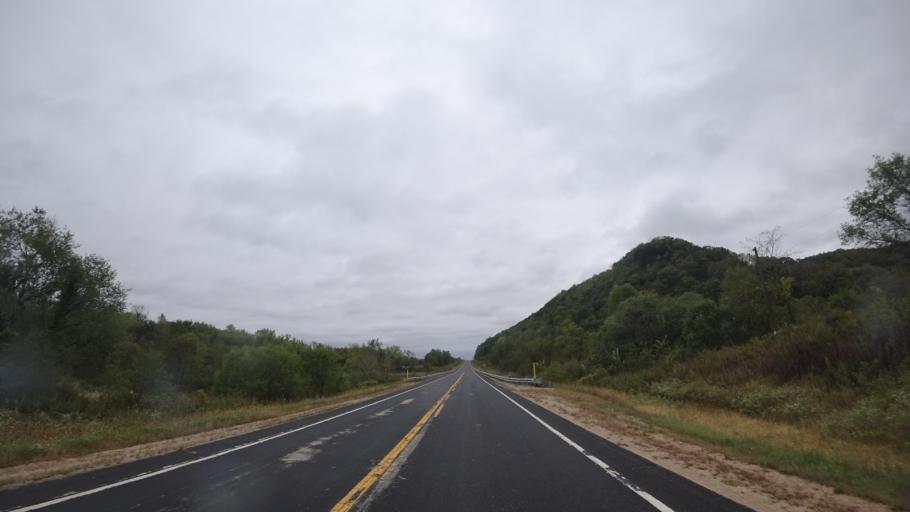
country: US
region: Wisconsin
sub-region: Grant County
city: Boscobel
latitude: 43.2012
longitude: -90.6501
